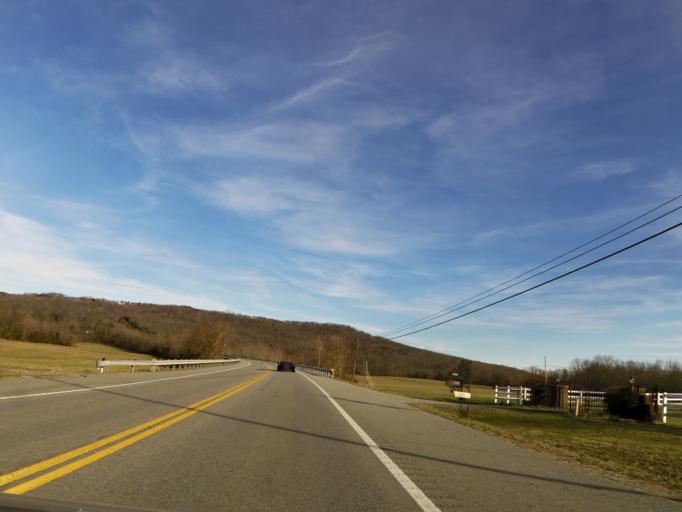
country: US
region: Tennessee
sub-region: White County
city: Sparta
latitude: 35.9216
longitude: -85.4110
